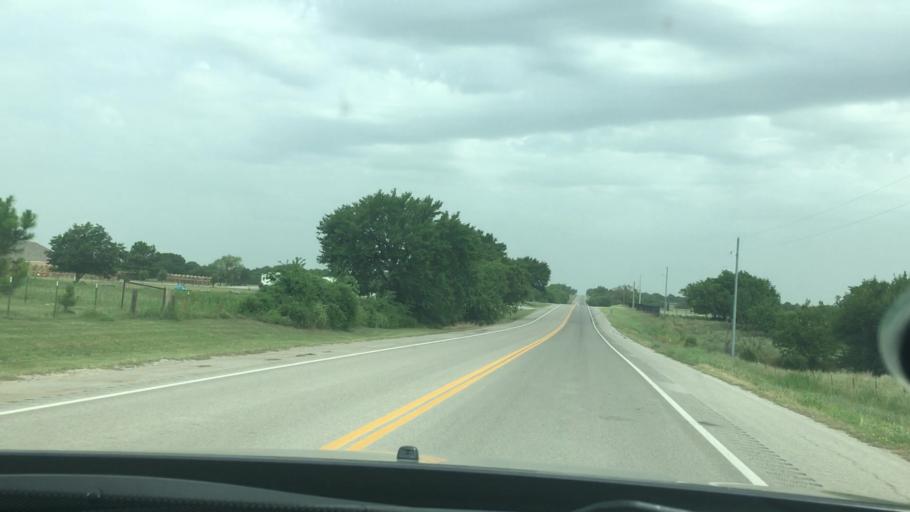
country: US
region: Oklahoma
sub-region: Garvin County
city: Pauls Valley
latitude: 34.8456
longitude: -97.2776
